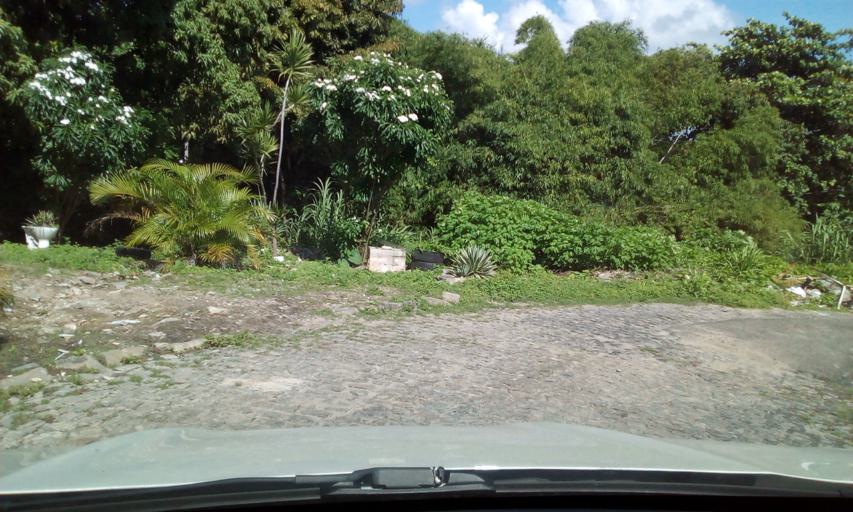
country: BR
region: Paraiba
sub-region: Joao Pessoa
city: Joao Pessoa
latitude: -7.1106
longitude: -34.8732
